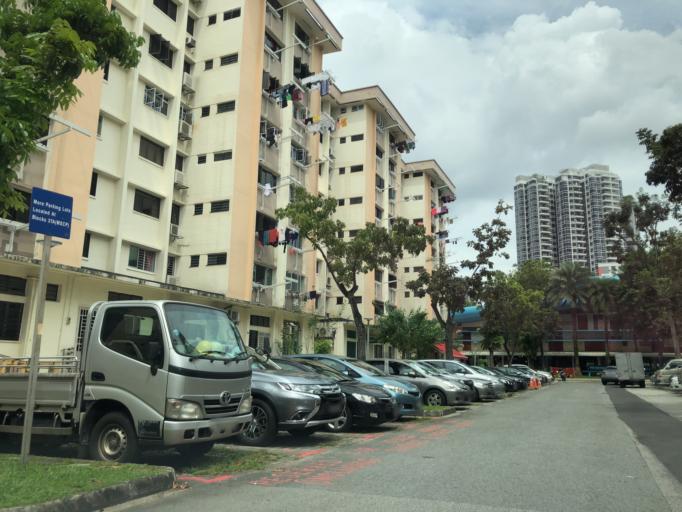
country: SG
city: Singapore
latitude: 1.3153
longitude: 103.8498
